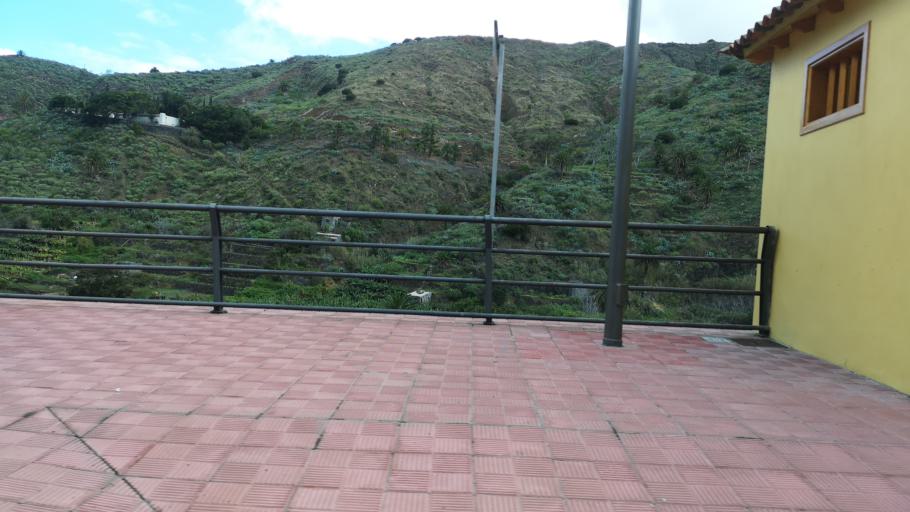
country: ES
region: Canary Islands
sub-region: Provincia de Santa Cruz de Tenerife
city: Hermigua
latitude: 28.1602
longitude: -17.1983
